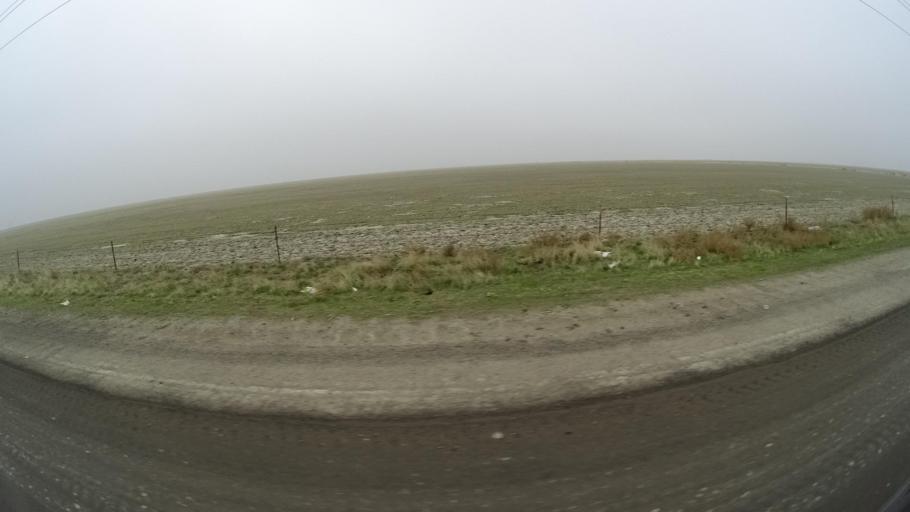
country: US
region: California
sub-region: Tulare County
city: Alpaugh
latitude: 35.7811
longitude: -119.4723
